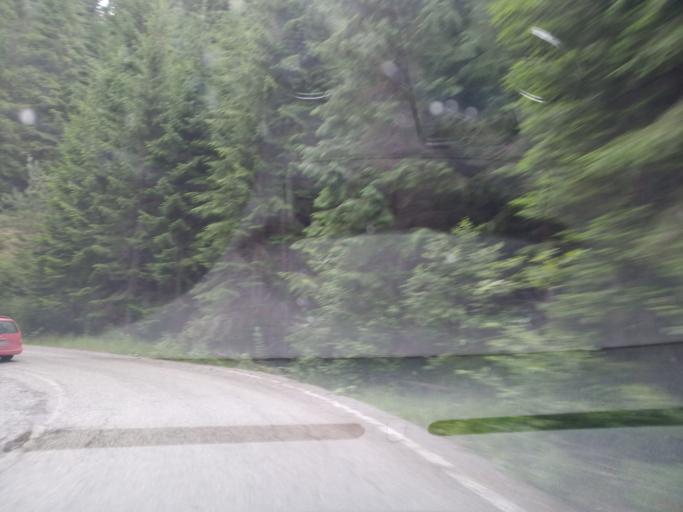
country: RO
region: Valcea
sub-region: Comuna Voineasa
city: Voineasa
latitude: 45.4220
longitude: 23.7406
